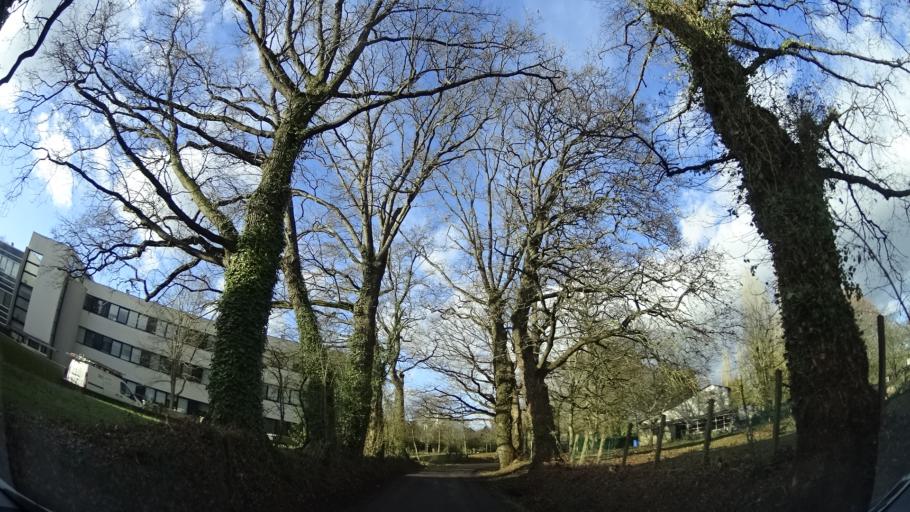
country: FR
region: Brittany
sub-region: Departement d'Ille-et-Vilaine
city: Cesson-Sevigne
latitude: 48.1330
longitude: -1.6354
